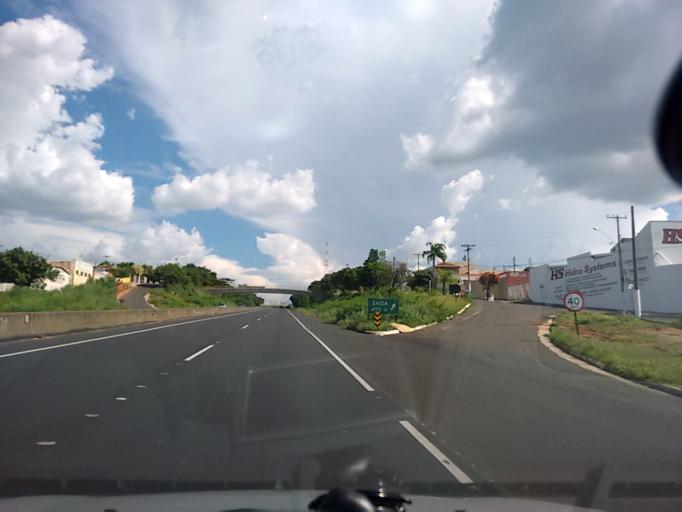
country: BR
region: Sao Paulo
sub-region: Marilia
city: Marilia
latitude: -22.2016
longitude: -49.9645
